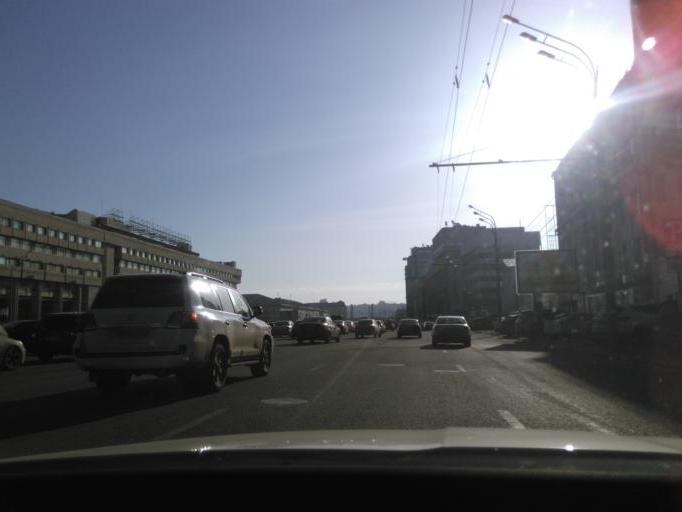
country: RU
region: Moskovskaya
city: Dorogomilovo
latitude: 55.7377
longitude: 37.5876
